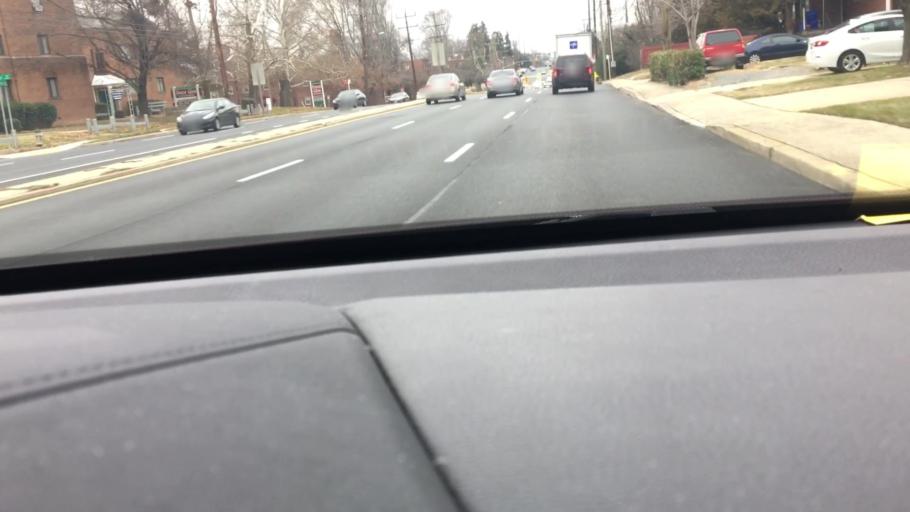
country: US
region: Maryland
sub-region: Montgomery County
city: Forest Glen
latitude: 39.0186
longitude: -77.0436
